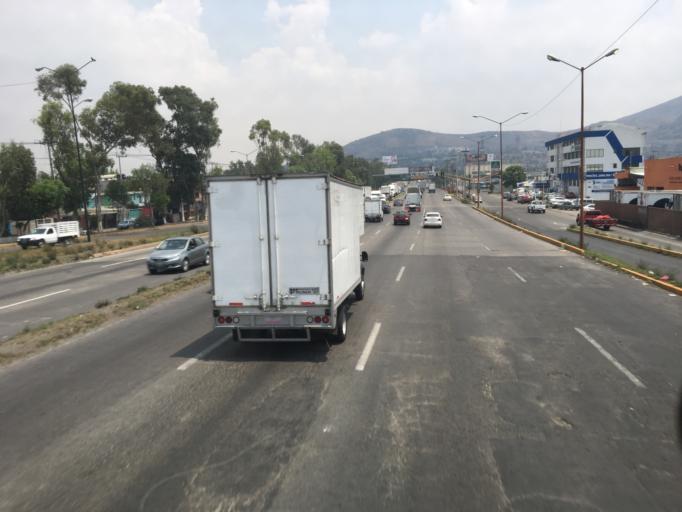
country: MX
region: Mexico
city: Tlalnepantla
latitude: 19.5482
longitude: -99.1835
